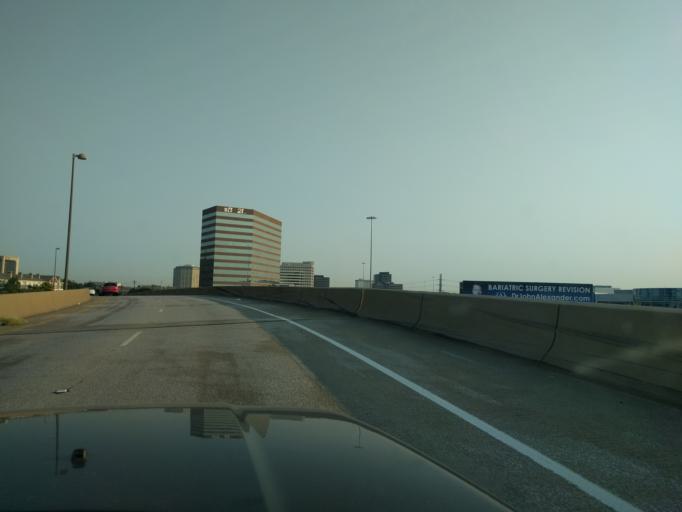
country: US
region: Texas
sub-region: Dallas County
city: Richardson
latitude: 32.9107
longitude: -96.7683
